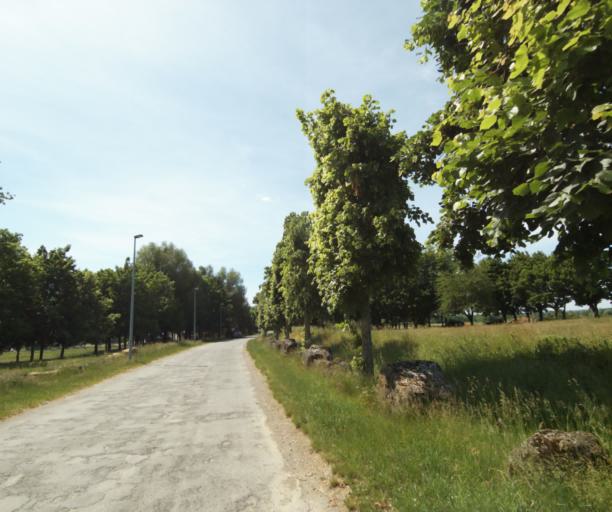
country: FR
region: Champagne-Ardenne
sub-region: Departement des Ardennes
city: Prix-les-Mezieres
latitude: 49.7603
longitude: 4.6870
